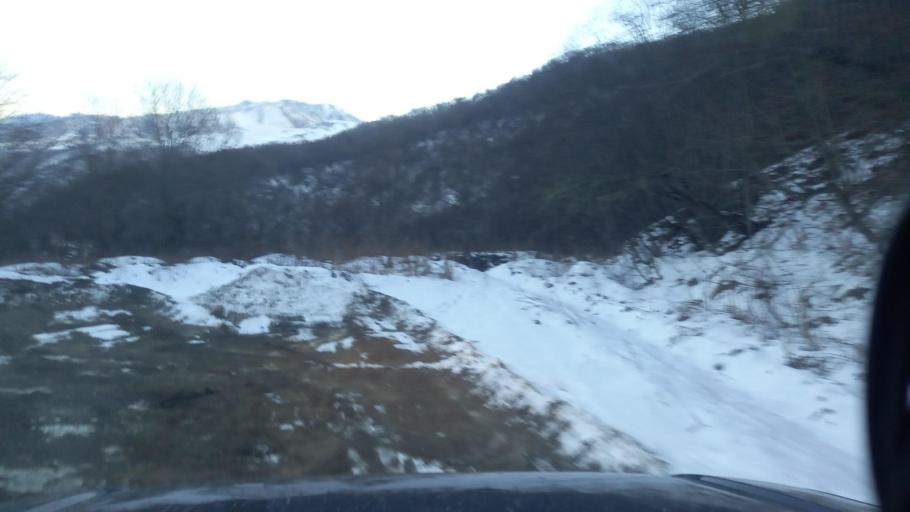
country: RU
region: Ingushetiya
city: Dzhayrakh
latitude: 42.8268
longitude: 44.5751
